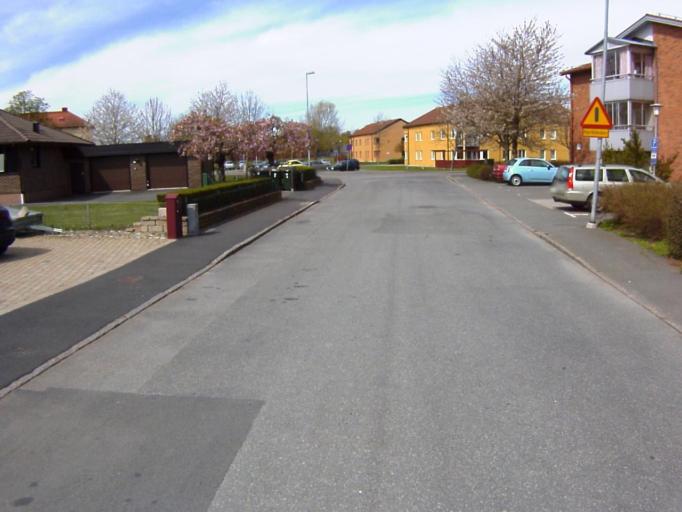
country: SE
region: Skane
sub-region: Kristianstads Kommun
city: Kristianstad
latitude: 56.0489
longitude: 14.1505
